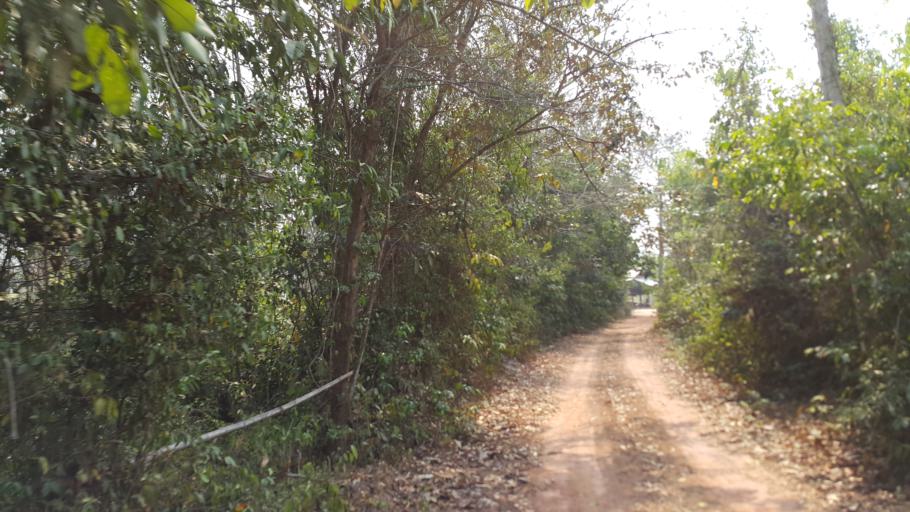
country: TH
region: Nakhon Phanom
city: Ban Phaeng
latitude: 17.8446
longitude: 104.2645
